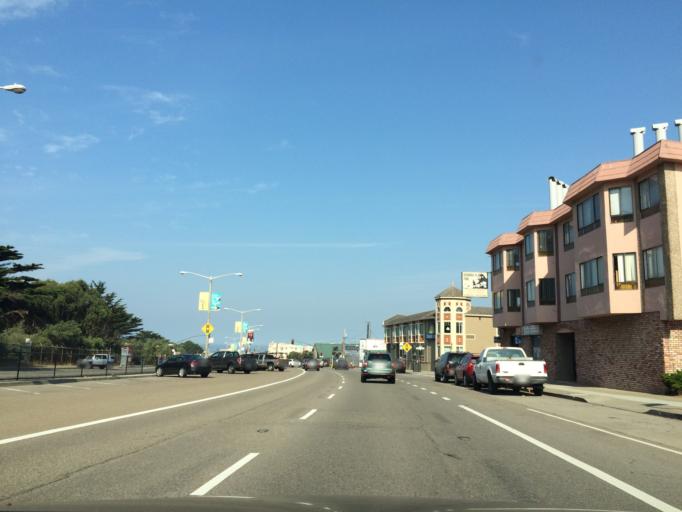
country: US
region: California
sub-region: San Mateo County
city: Daly City
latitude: 37.7354
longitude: -122.5014
